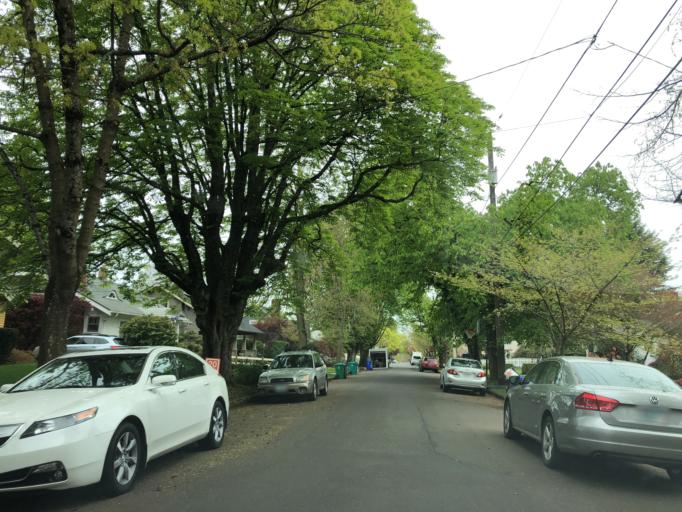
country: US
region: Oregon
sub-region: Multnomah County
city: Portland
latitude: 45.5533
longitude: -122.6317
